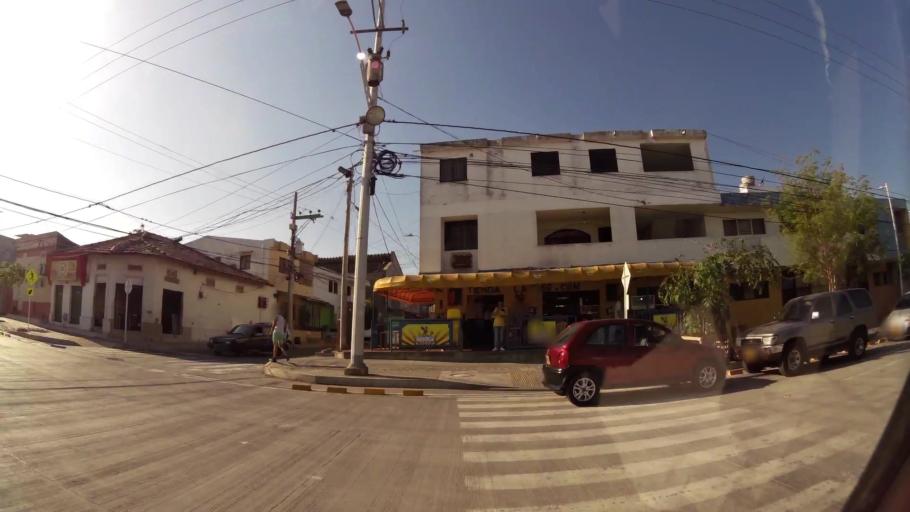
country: CO
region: Atlantico
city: Barranquilla
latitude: 10.9899
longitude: -74.7847
